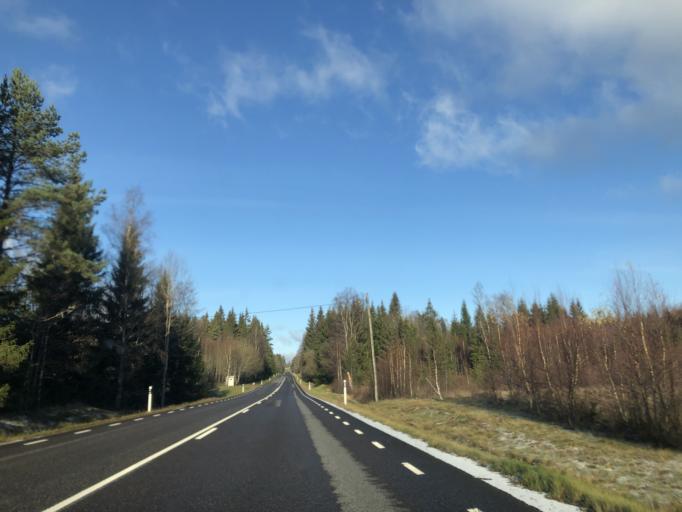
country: SE
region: Vaestra Goetaland
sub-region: Tranemo Kommun
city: Limmared
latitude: 57.6465
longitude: 13.4412
